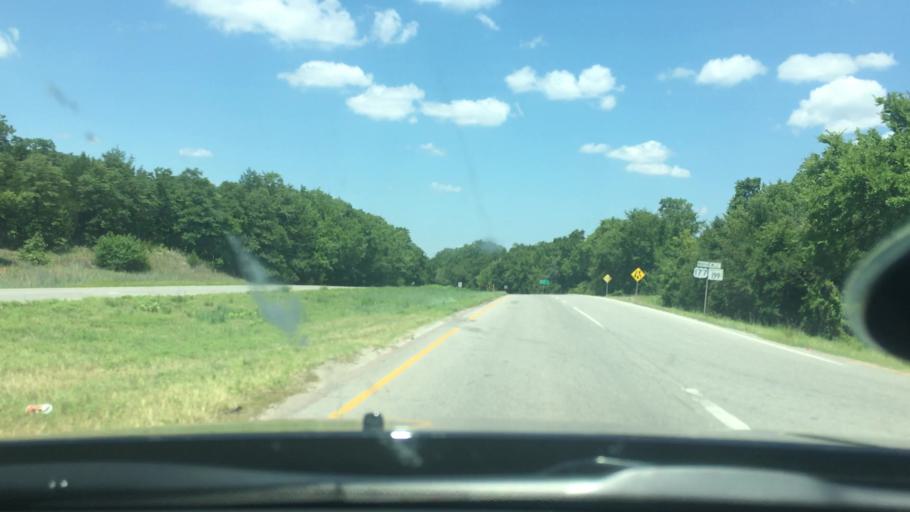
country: US
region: Oklahoma
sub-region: Marshall County
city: Oakland
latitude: 34.1700
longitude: -96.8340
